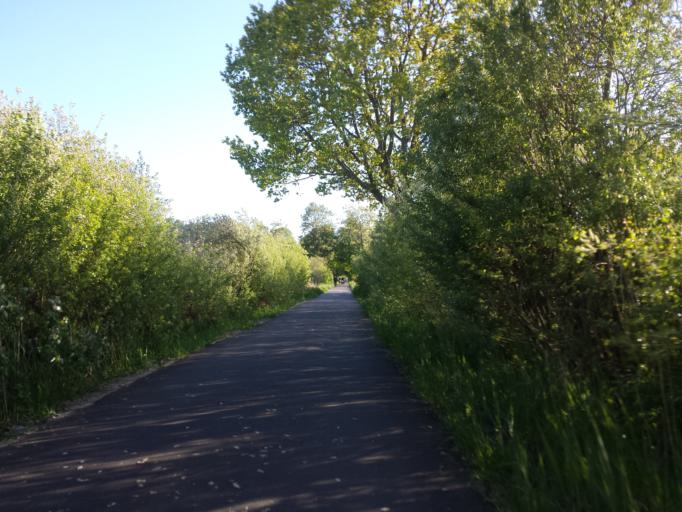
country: DE
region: Lower Saxony
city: Lilienthal
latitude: 53.1233
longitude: 8.8857
